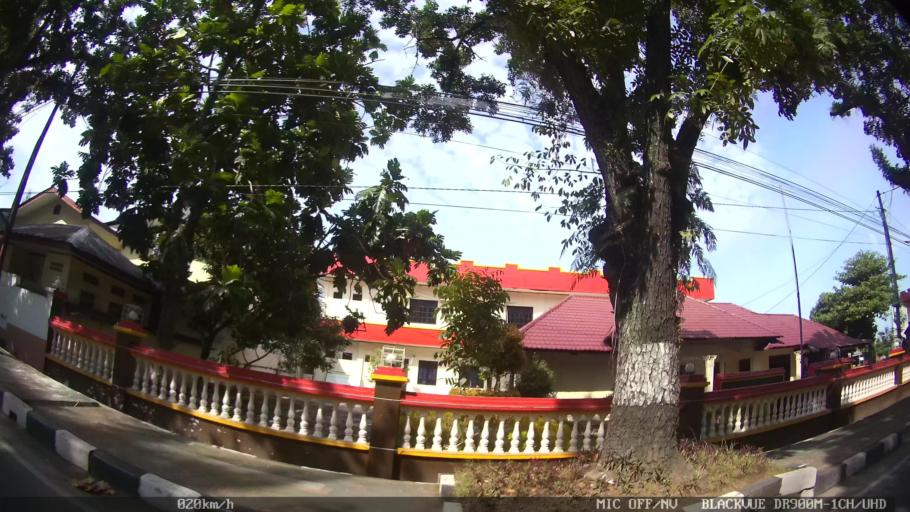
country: ID
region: North Sumatra
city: Medan
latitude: 3.5733
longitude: 98.6589
